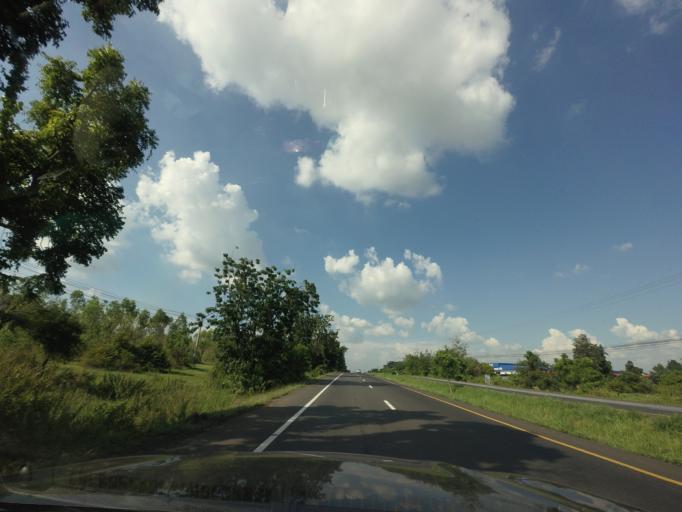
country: TH
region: Nakhon Ratchasima
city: Bua Lai
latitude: 15.6964
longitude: 102.5823
